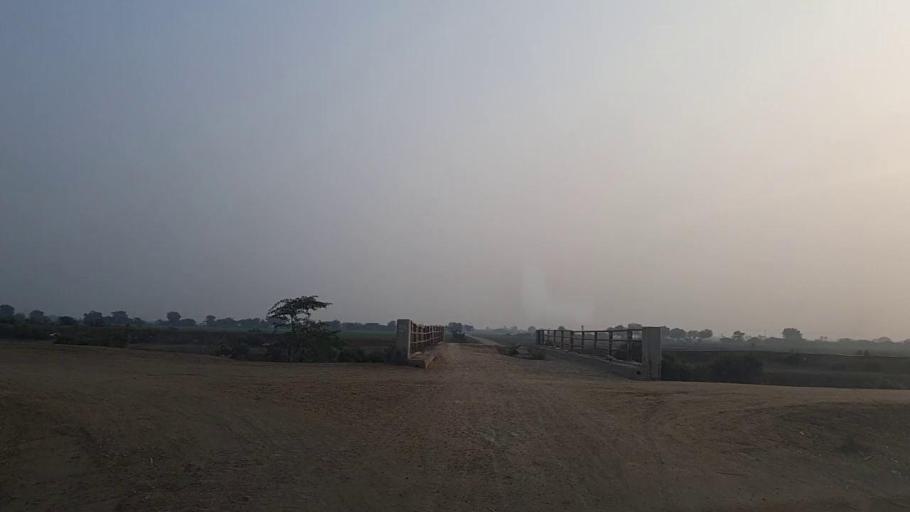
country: PK
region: Sindh
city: Sinjhoro
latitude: 26.0923
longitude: 68.7972
